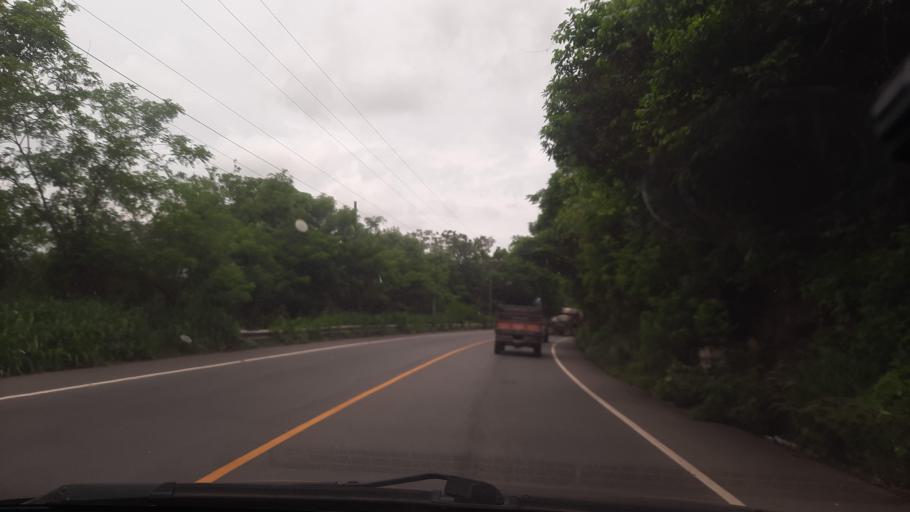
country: GT
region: Zacapa
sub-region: Municipio de Zacapa
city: Gualan
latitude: 15.1571
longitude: -89.3224
